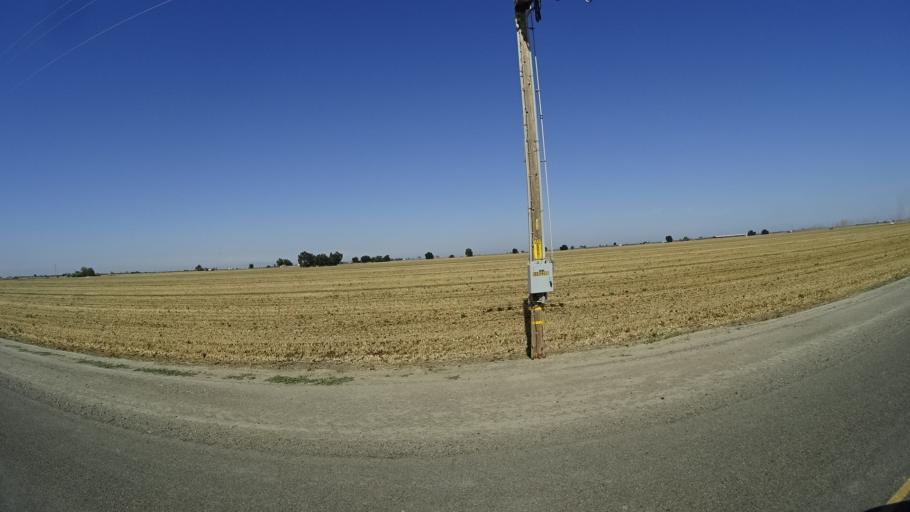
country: US
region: California
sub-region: Kings County
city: Home Garden
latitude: 36.2290
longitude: -119.5563
